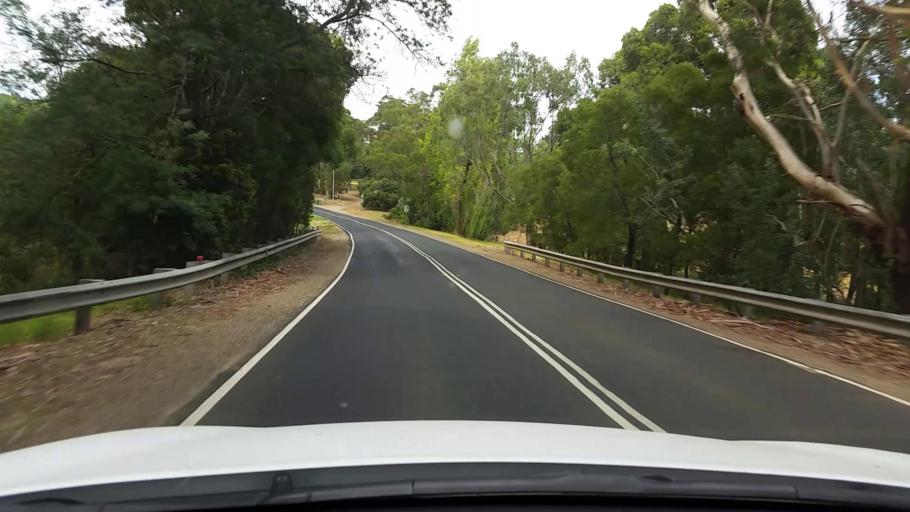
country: AU
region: Victoria
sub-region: Mornington Peninsula
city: Merricks
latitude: -38.4287
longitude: 145.0419
